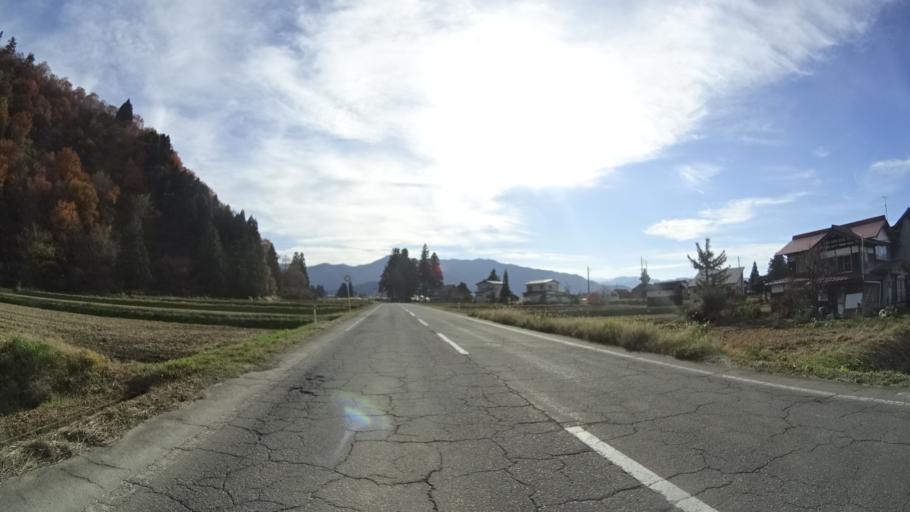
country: JP
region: Niigata
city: Shiozawa
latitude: 37.0252
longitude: 138.8813
